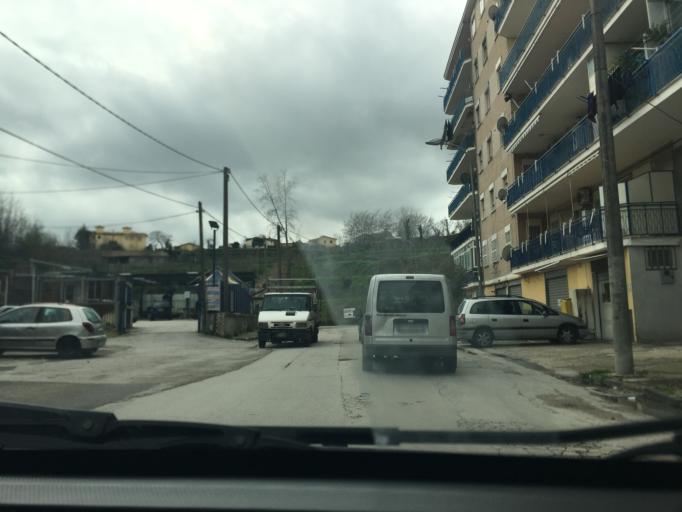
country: IT
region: Campania
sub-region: Provincia di Napoli
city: Mugnano di Napoli
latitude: 40.8951
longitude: 14.2026
